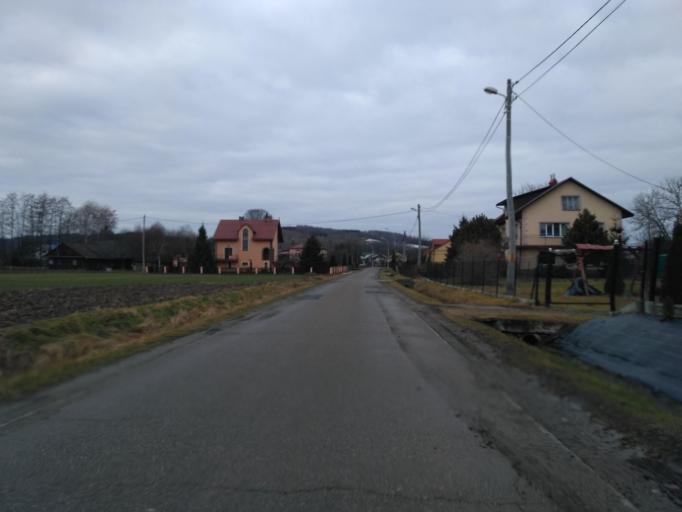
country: PL
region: Subcarpathian Voivodeship
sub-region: Powiat przemyski
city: Przedmiescie Dubieckie
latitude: 49.8299
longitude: 22.3778
